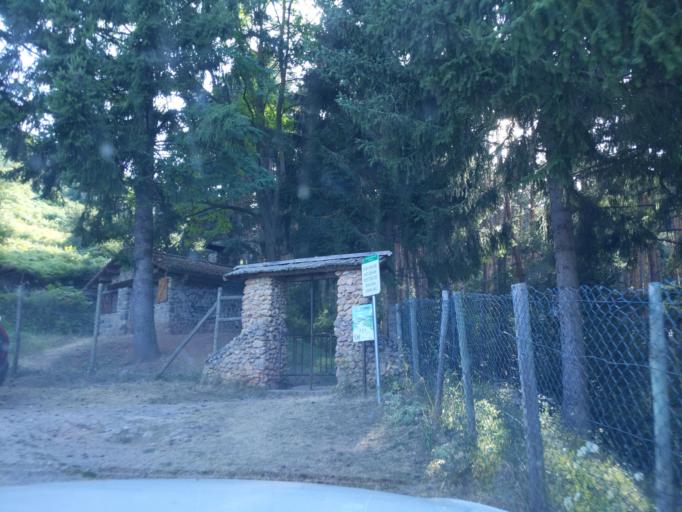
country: ES
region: La Rioja
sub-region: Provincia de La Rioja
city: Zorraquin
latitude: 42.3172
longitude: -3.0281
